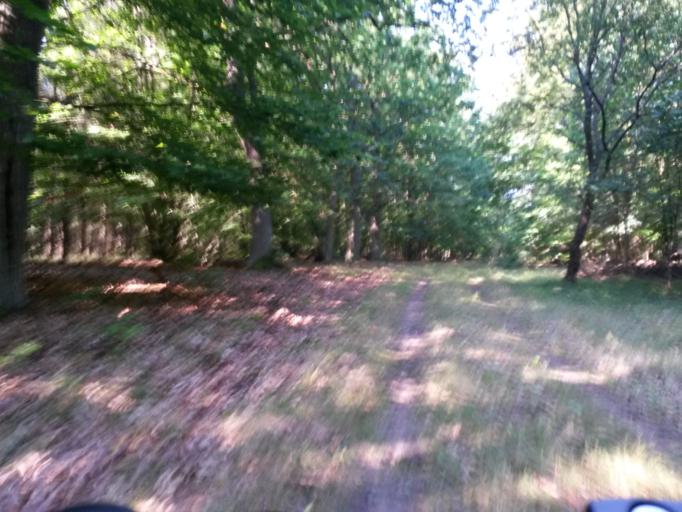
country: DE
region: Brandenburg
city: Zehdenick
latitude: 53.0572
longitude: 13.4017
